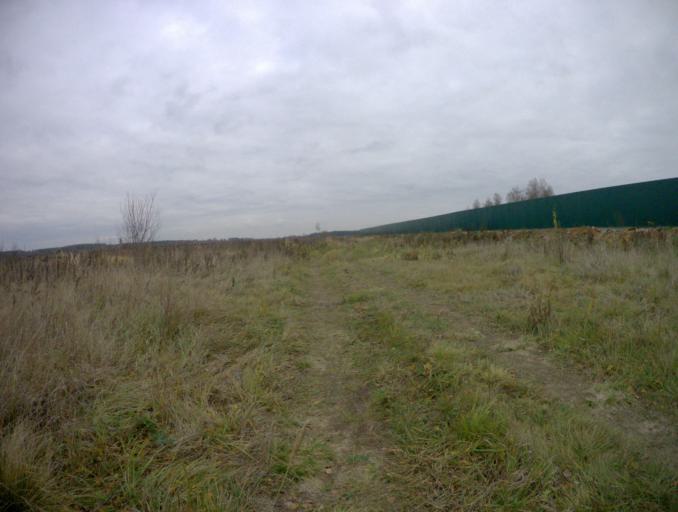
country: RU
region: Moskovskaya
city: Malaya Dubna
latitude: 55.9904
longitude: 38.9763
